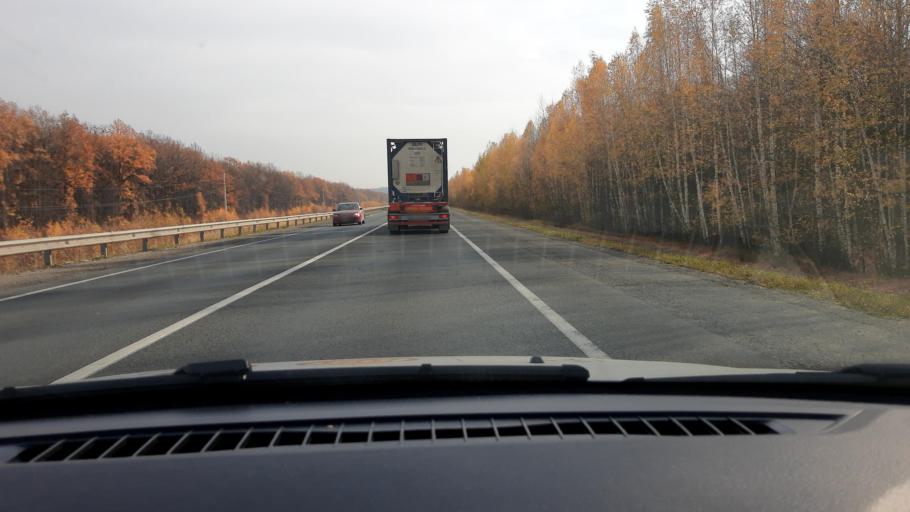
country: RU
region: Nizjnij Novgorod
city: Pamyat' Parizhskoy Kommuny
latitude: 56.0838
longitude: 44.3515
